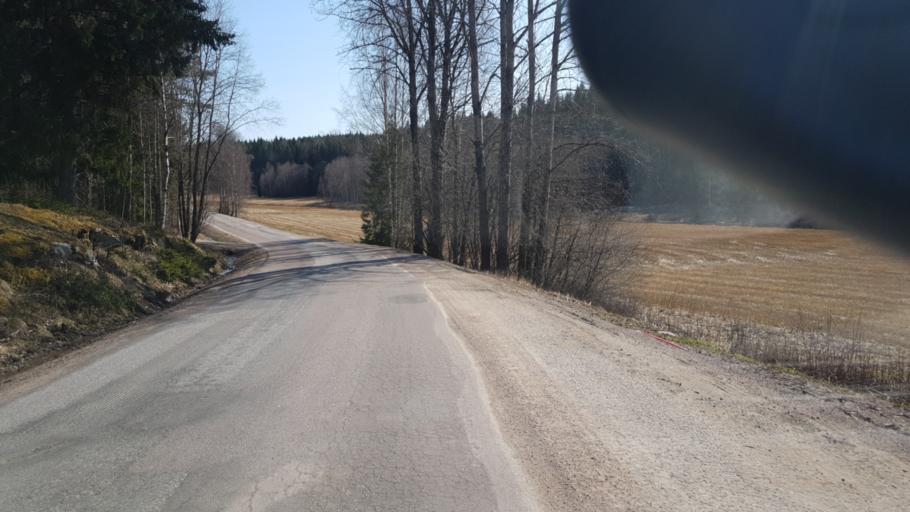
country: SE
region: Vaermland
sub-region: Arvika Kommun
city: Arvika
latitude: 59.6469
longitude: 12.8073
